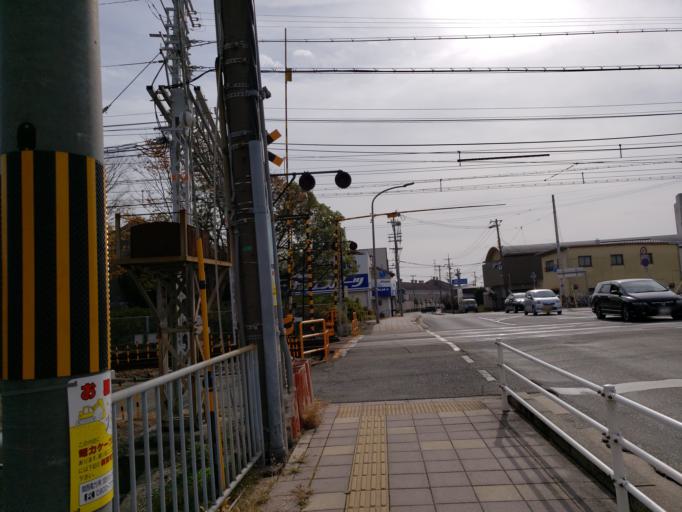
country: JP
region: Hyogo
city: Kakogawacho-honmachi
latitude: 34.7523
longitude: 134.8042
